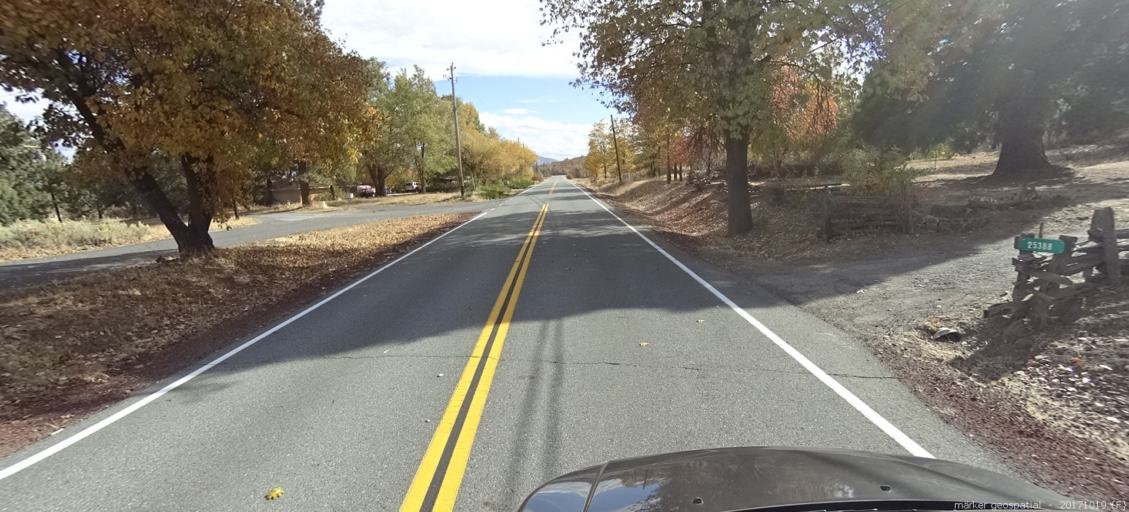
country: US
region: California
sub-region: Shasta County
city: Burney
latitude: 41.0186
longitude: -121.4713
